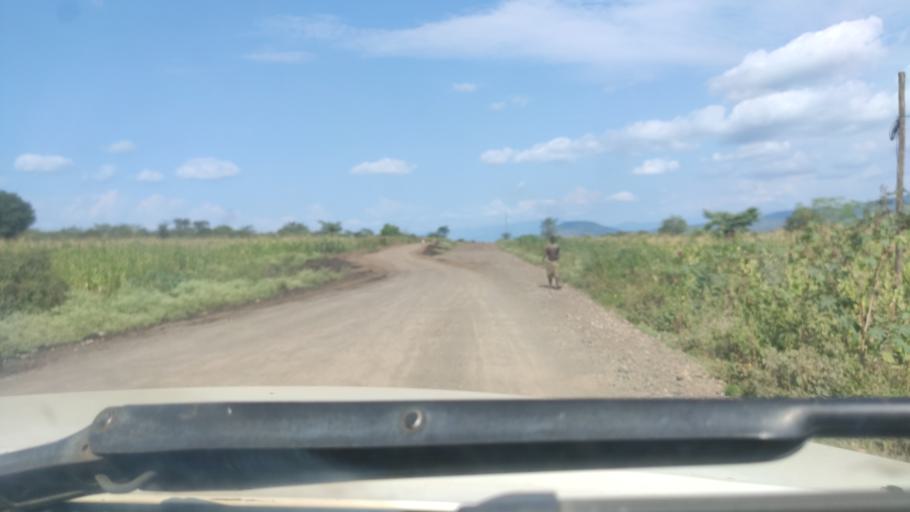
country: ET
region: Southern Nations, Nationalities, and People's Region
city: Felege Neway
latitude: 6.3949
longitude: 37.1039
